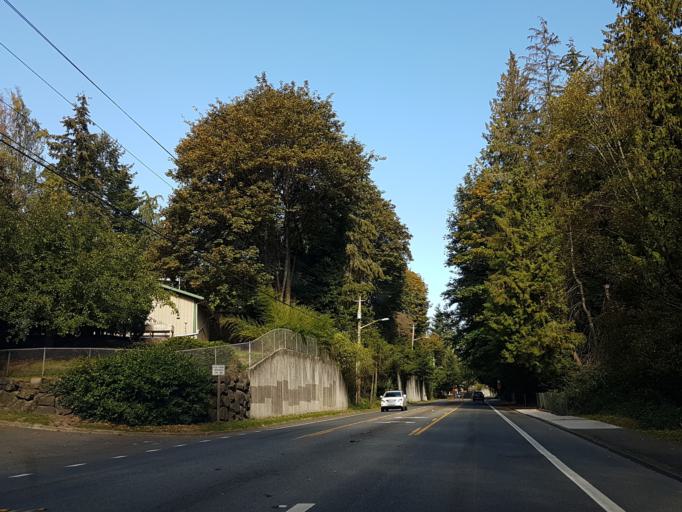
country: US
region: Washington
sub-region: King County
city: Lake Forest Park
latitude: 47.7631
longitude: -122.2641
